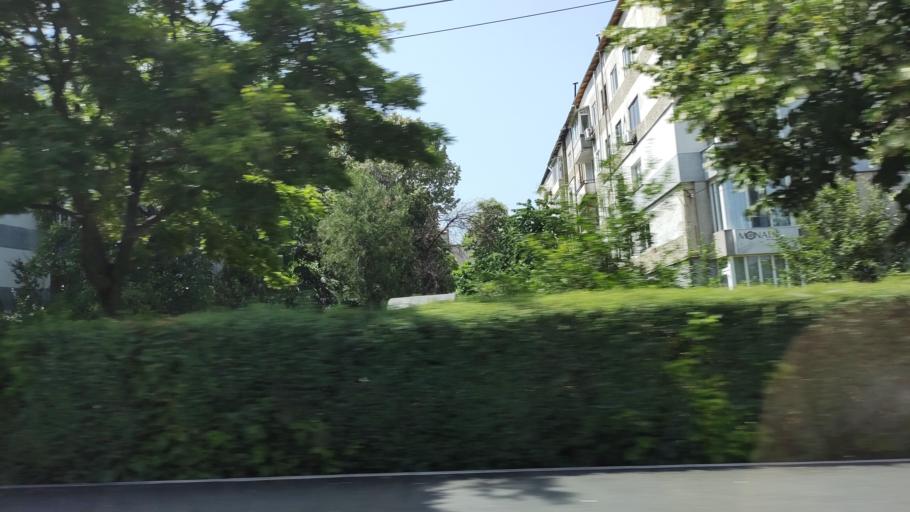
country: RO
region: Mehedinti
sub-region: Municipiul Orsova
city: Orsova
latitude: 44.7259
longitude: 22.3992
